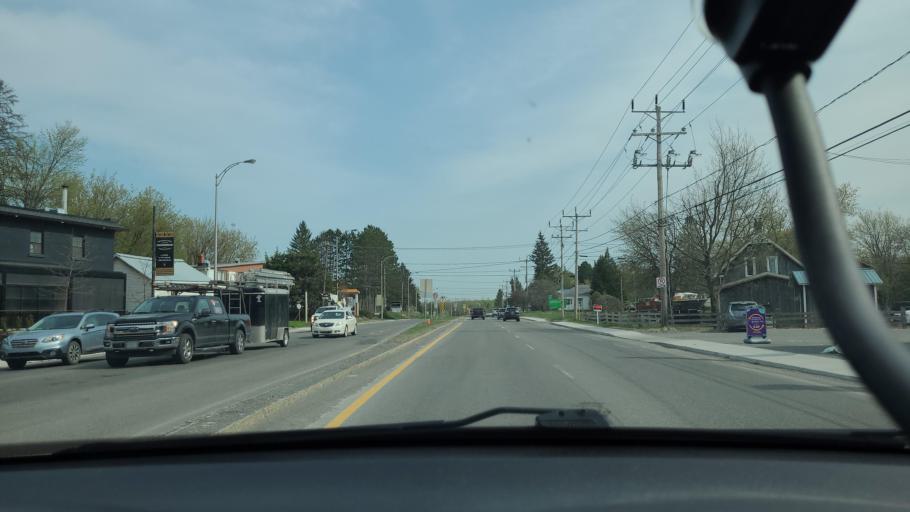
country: CA
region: Quebec
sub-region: Laurentides
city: Prevost
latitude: 45.8729
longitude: -74.0769
